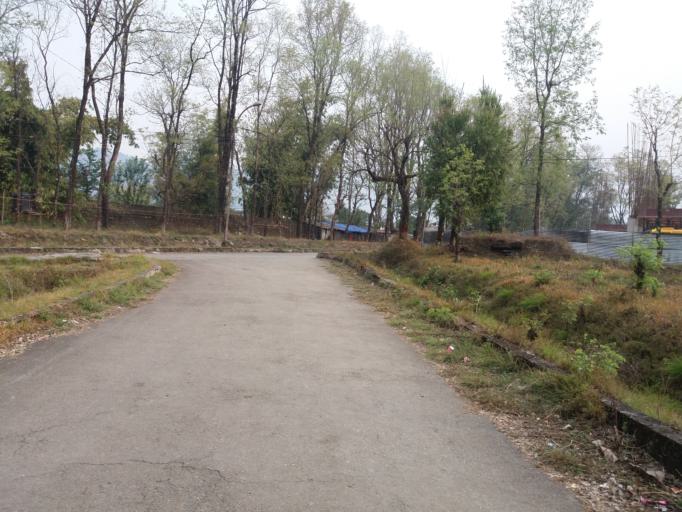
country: NP
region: Western Region
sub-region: Gandaki Zone
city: Pokhara
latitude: 28.2546
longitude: 83.9758
